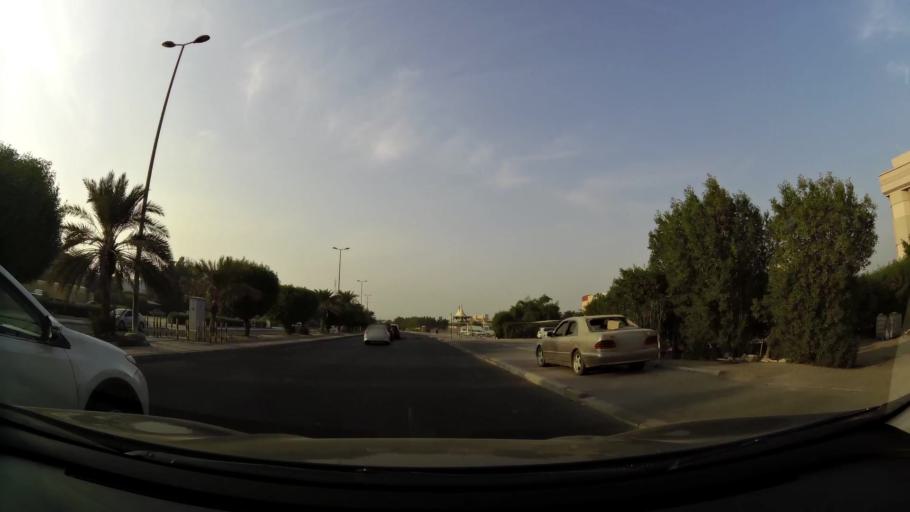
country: KW
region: Mubarak al Kabir
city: Sabah as Salim
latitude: 29.2460
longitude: 48.0697
